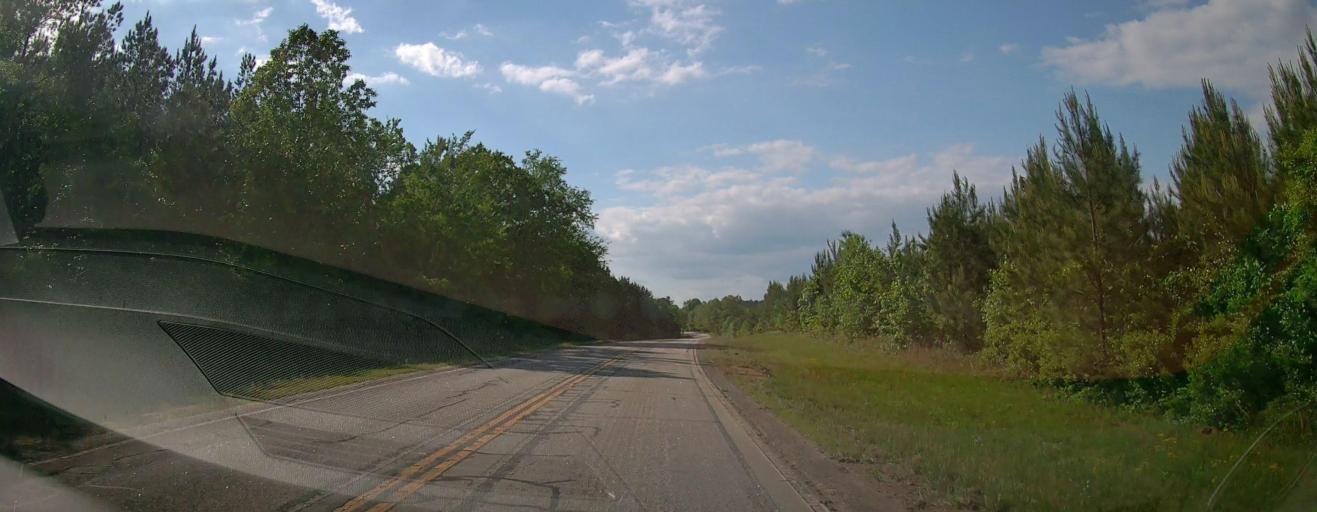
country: US
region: Georgia
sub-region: Wilkinson County
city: Irwinton
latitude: 32.9282
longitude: -83.0121
